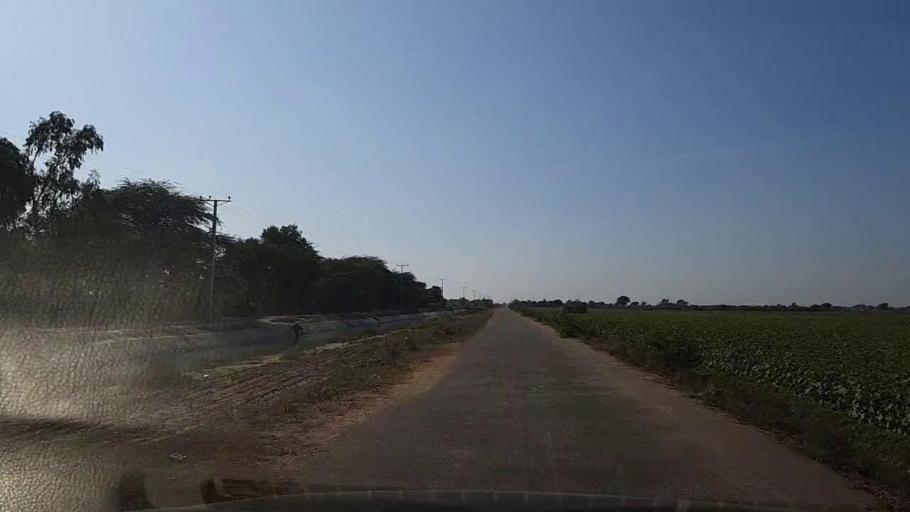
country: PK
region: Sindh
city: Thatta
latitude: 24.5966
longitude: 67.8118
